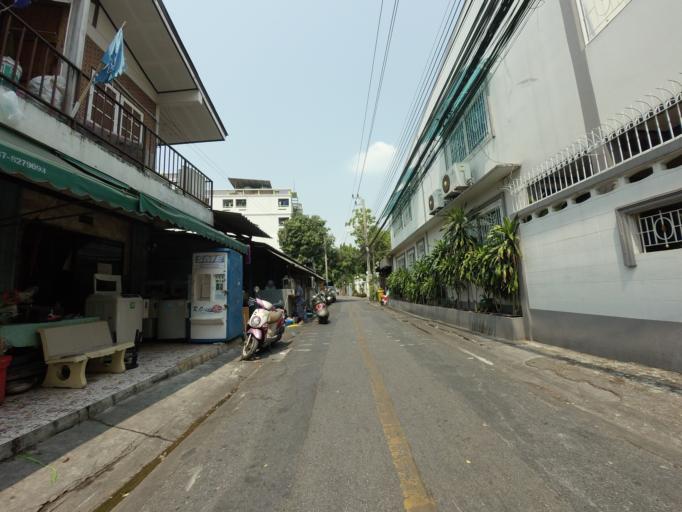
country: TH
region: Bangkok
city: Din Daeng
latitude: 13.7667
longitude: 100.5651
